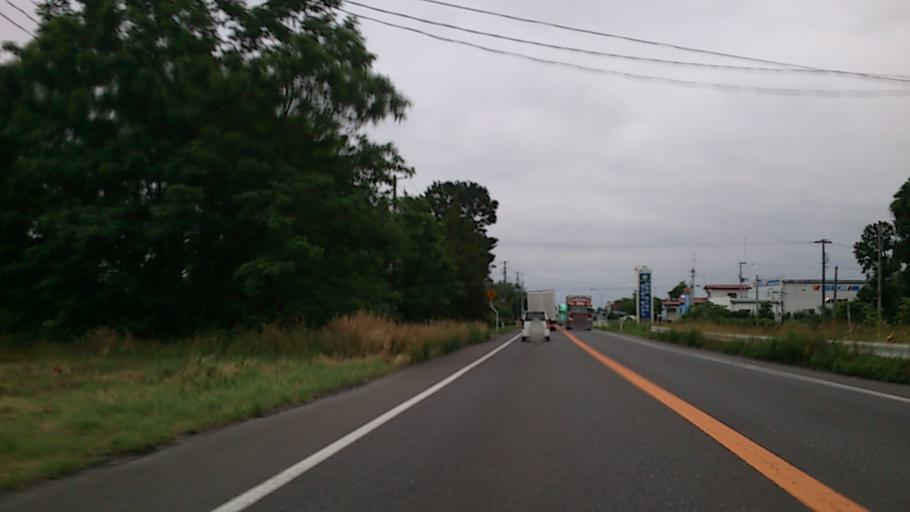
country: JP
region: Fukushima
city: Sukagawa
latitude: 37.2245
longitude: 140.3299
